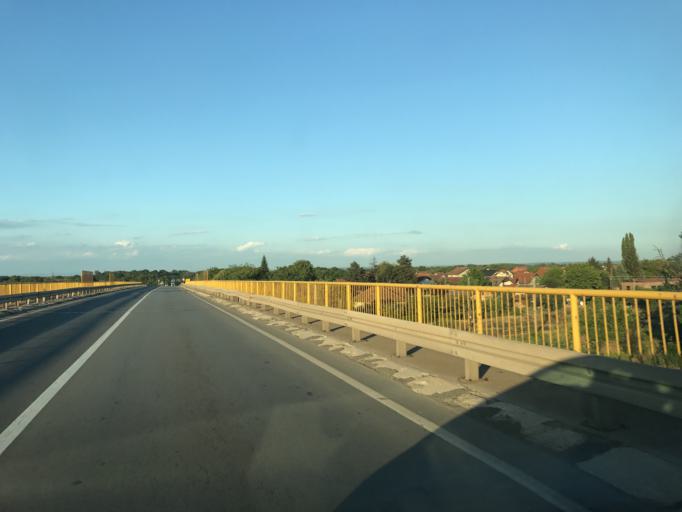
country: RS
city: Lugavcina
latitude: 44.5877
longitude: 20.9976
